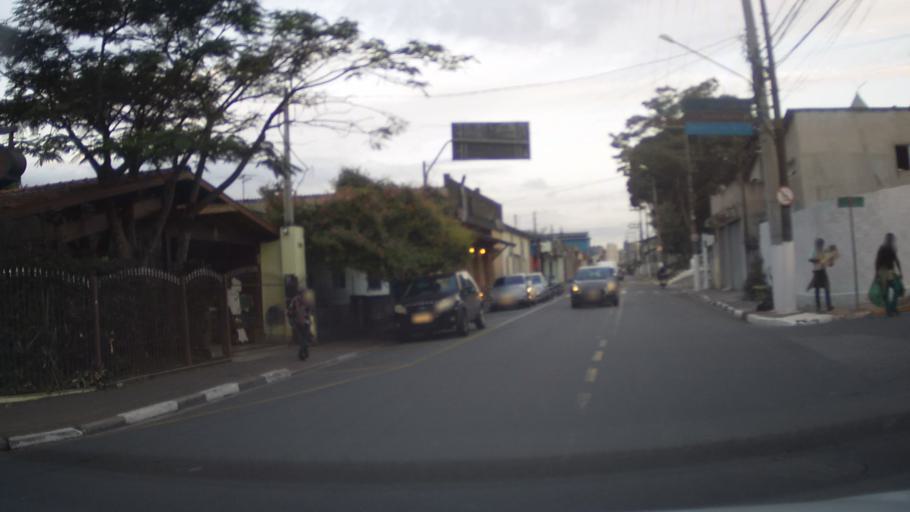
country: BR
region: Sao Paulo
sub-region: Aruja
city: Aruja
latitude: -23.3961
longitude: -46.3274
